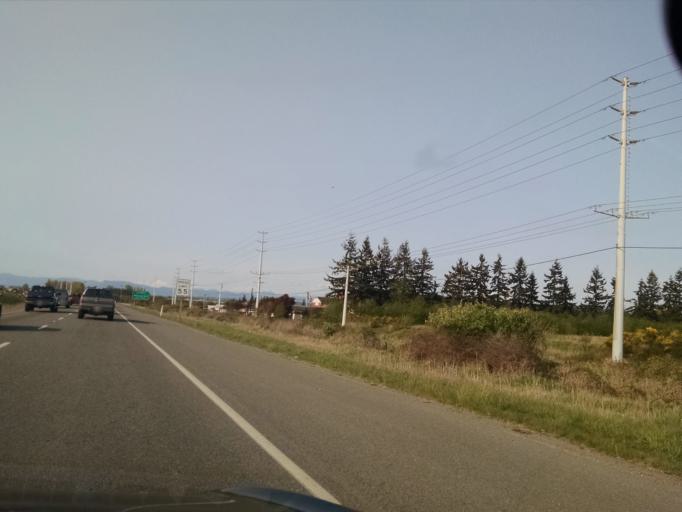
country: US
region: Washington
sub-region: Snohomish County
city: Marysville
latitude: 48.0240
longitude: -122.1853
